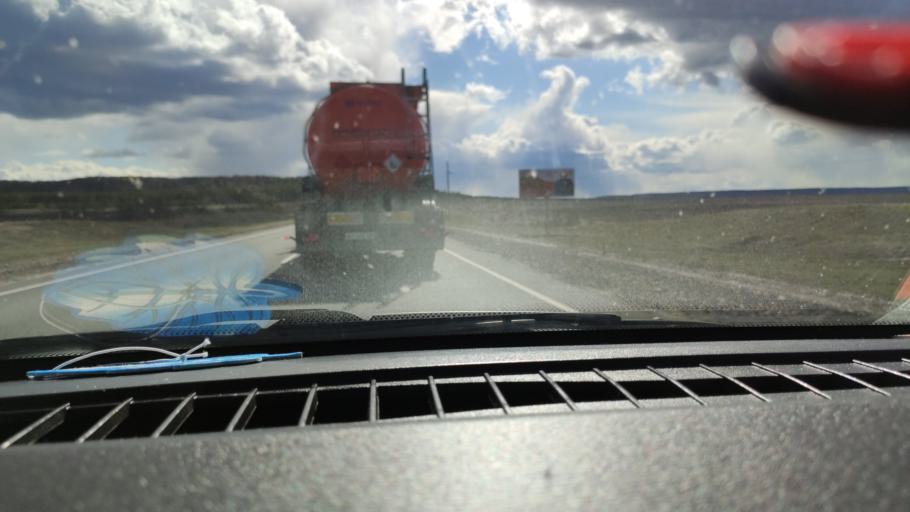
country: RU
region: Saratov
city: Khvalynsk
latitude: 52.5465
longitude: 48.0683
